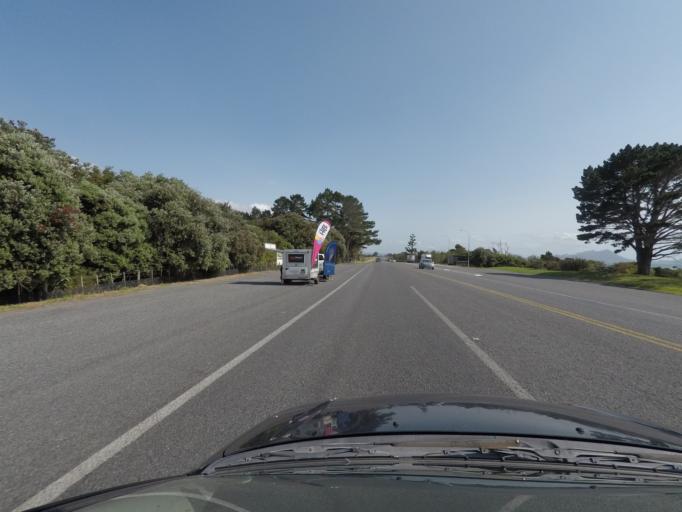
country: NZ
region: Northland
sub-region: Whangarei
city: Ruakaka
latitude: -35.9353
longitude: 174.4556
